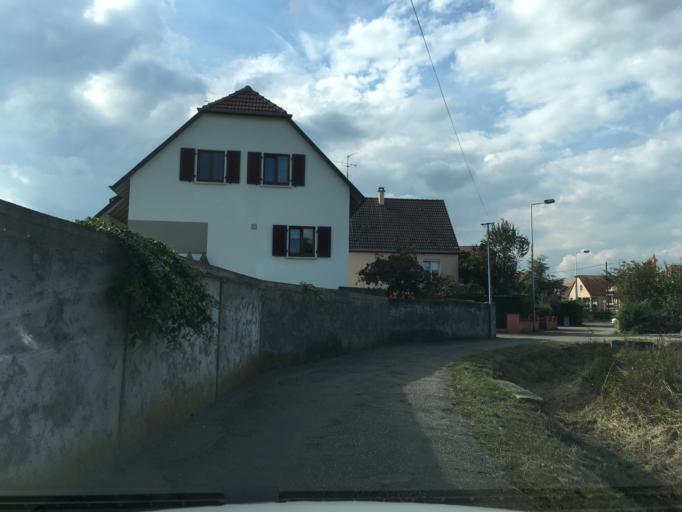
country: FR
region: Alsace
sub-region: Departement du Haut-Rhin
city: Colmar
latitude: 48.0735
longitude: 7.3705
